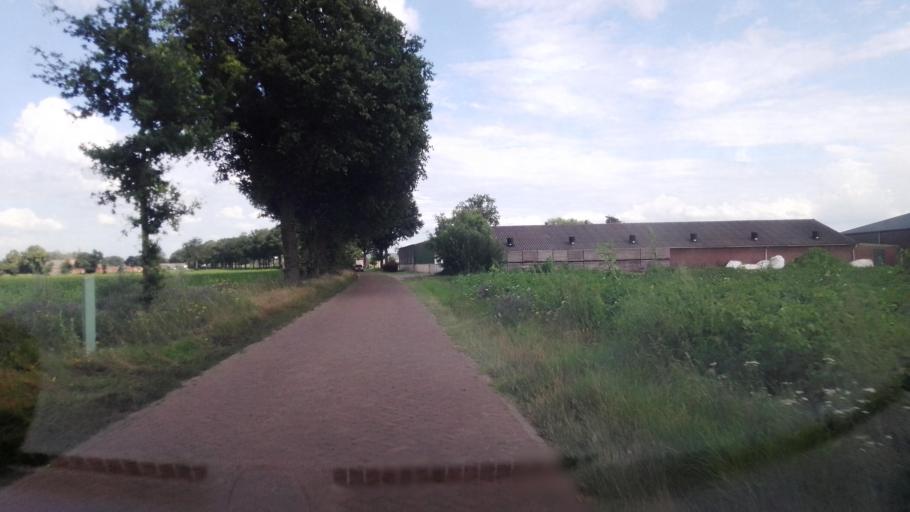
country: NL
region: Limburg
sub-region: Gemeente Peel en Maas
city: Maasbree
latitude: 51.3570
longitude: 6.0262
